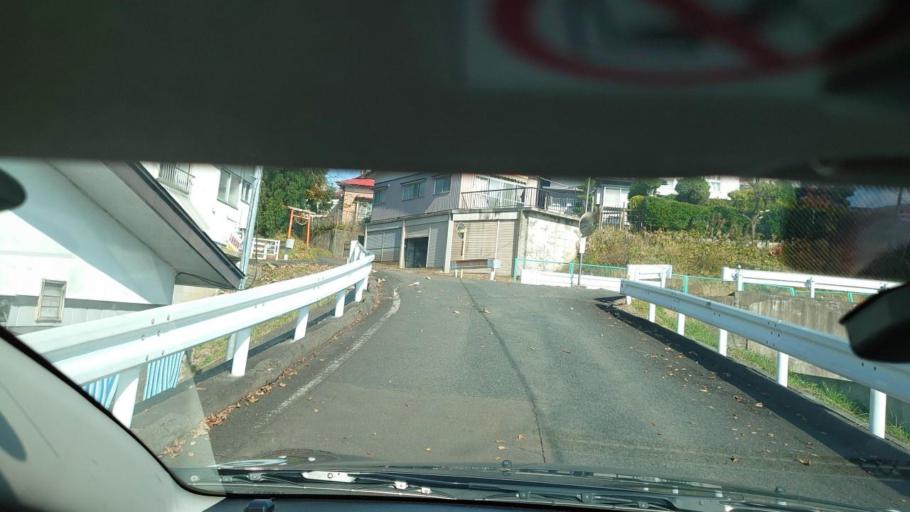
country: JP
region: Iwate
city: Hanamaki
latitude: 39.4482
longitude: 141.0719
